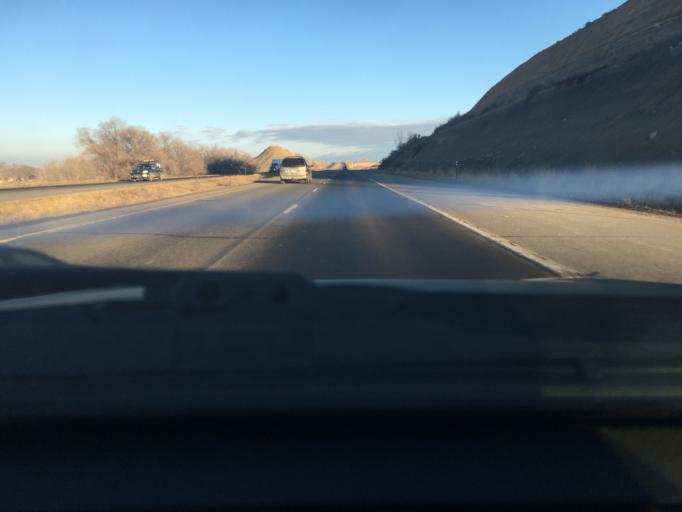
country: US
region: Colorado
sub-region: Montrose County
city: Montrose
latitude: 38.5323
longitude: -107.9370
